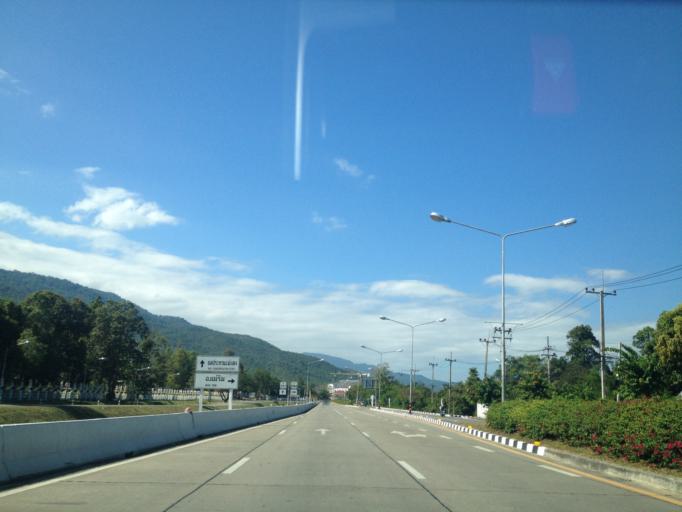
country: TH
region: Chiang Mai
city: Chiang Mai
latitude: 18.8428
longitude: 98.9639
